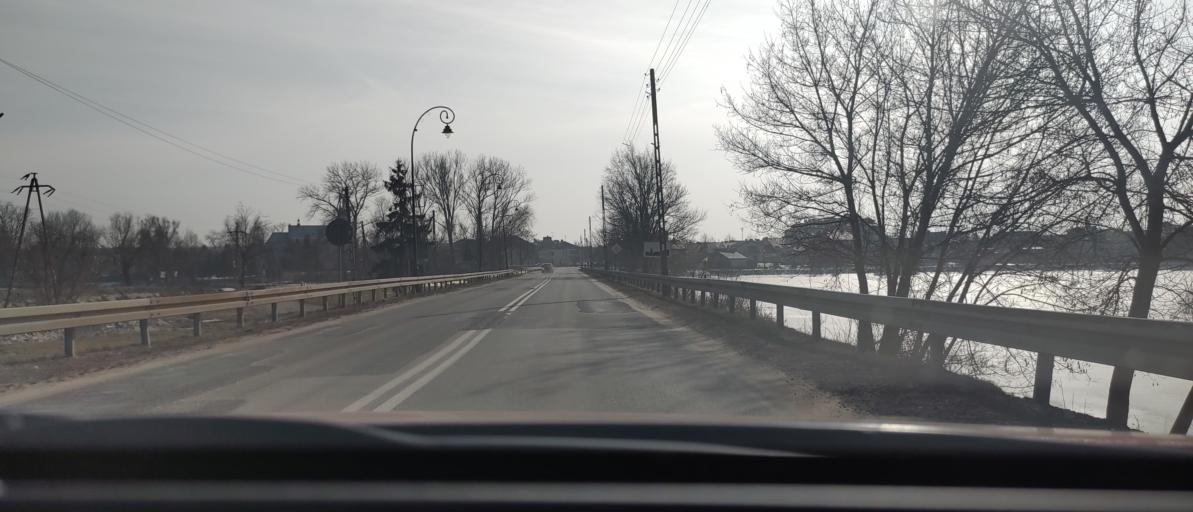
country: PL
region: Masovian Voivodeship
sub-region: Powiat bialobrzeski
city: Bialobrzegi
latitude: 51.6545
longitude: 20.9515
